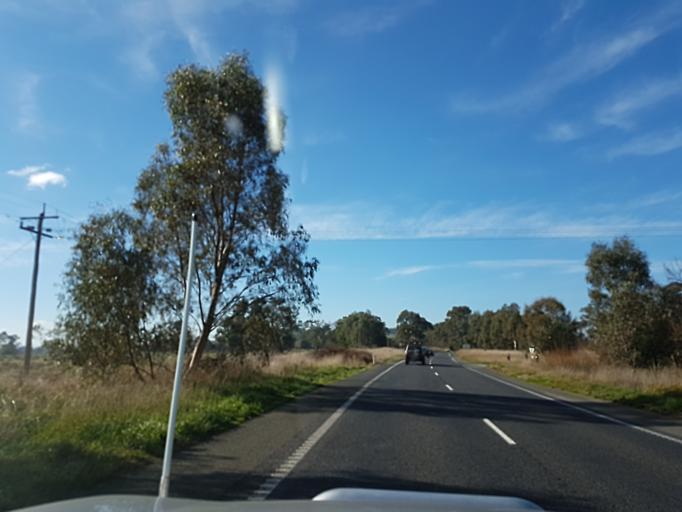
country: AU
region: Victoria
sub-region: Murrindindi
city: Alexandra
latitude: -37.1527
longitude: 145.5768
